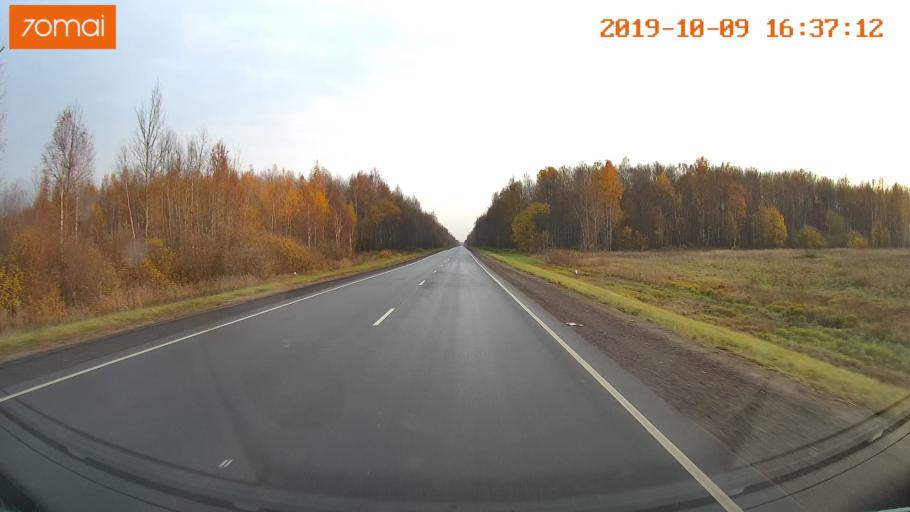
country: RU
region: Kostroma
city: Volgorechensk
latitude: 57.5304
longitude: 41.0218
